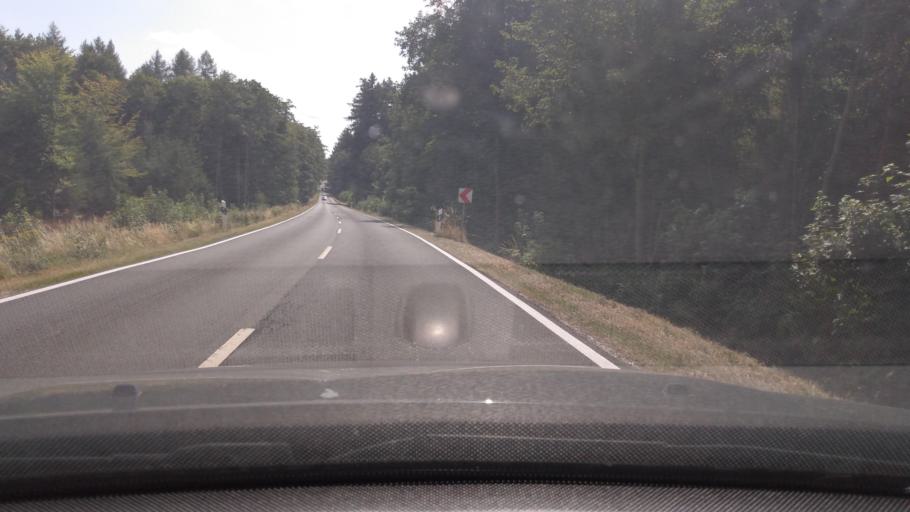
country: DE
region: Rheinland-Pfalz
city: Lotzbeuren
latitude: 49.9100
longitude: 7.2079
